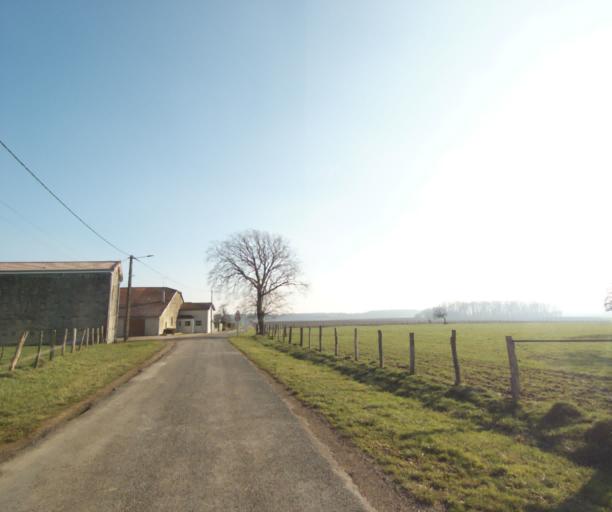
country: FR
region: Champagne-Ardenne
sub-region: Departement de la Haute-Marne
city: Bienville
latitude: 48.5050
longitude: 5.0370
